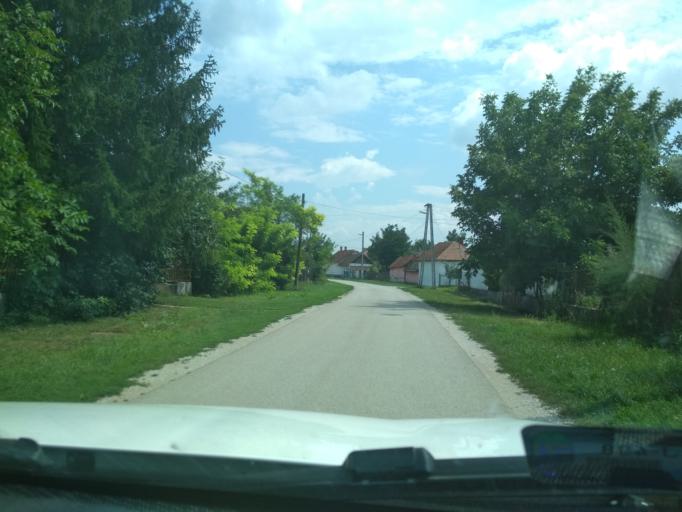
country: HU
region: Jasz-Nagykun-Szolnok
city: Abadszalok
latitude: 47.4756
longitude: 20.6047
